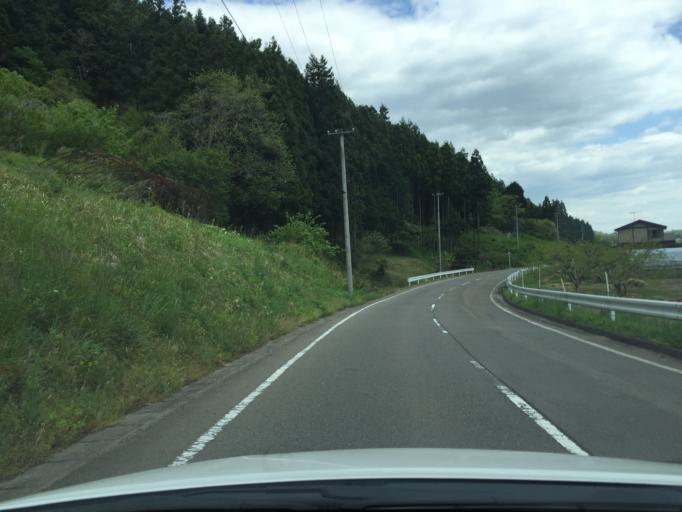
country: JP
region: Fukushima
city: Hobaramachi
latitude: 37.7581
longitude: 140.5698
